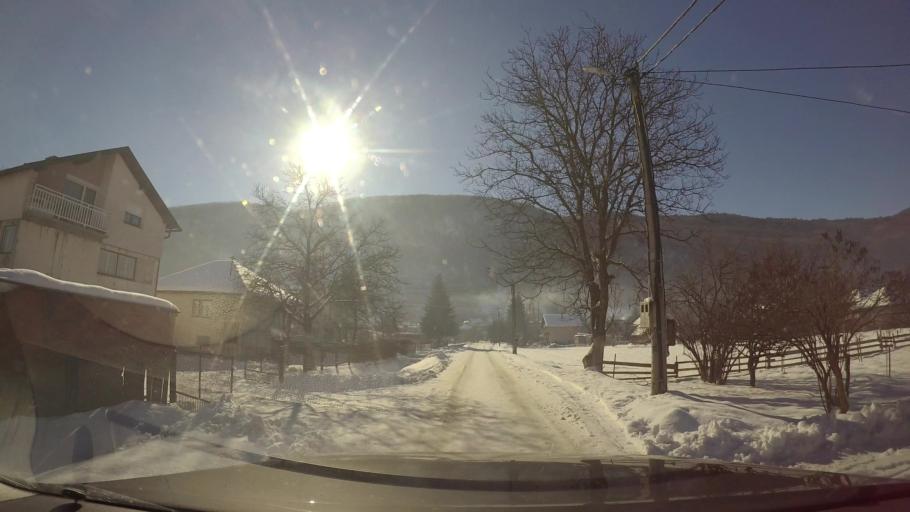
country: BA
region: Federation of Bosnia and Herzegovina
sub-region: Kanton Sarajevo
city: Sarajevo
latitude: 43.7904
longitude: 18.3381
